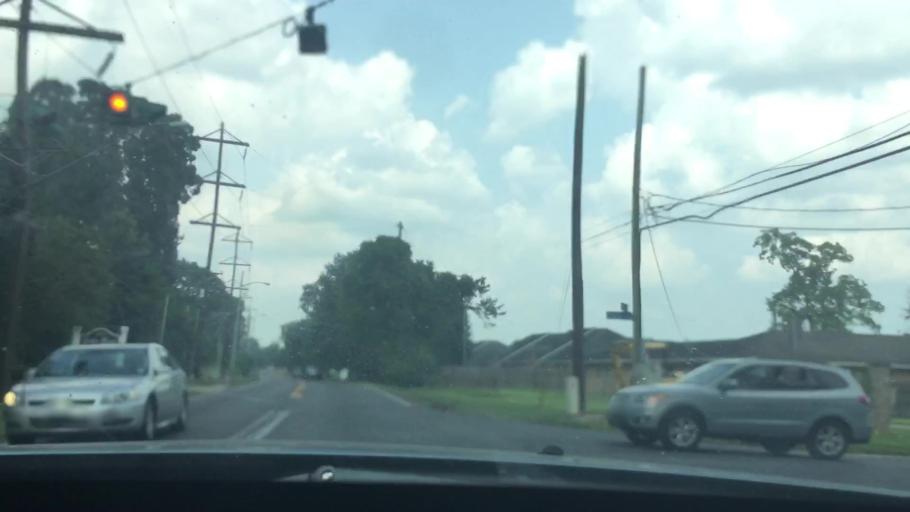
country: US
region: Louisiana
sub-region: East Baton Rouge Parish
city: Monticello
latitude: 30.4408
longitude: -91.0441
